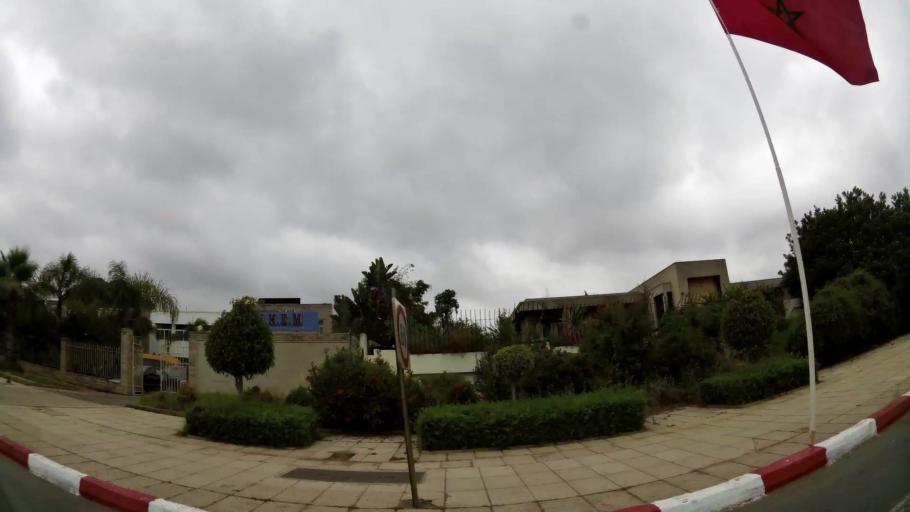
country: MA
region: Rabat-Sale-Zemmour-Zaer
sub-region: Rabat
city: Rabat
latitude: 33.9685
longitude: -6.8284
